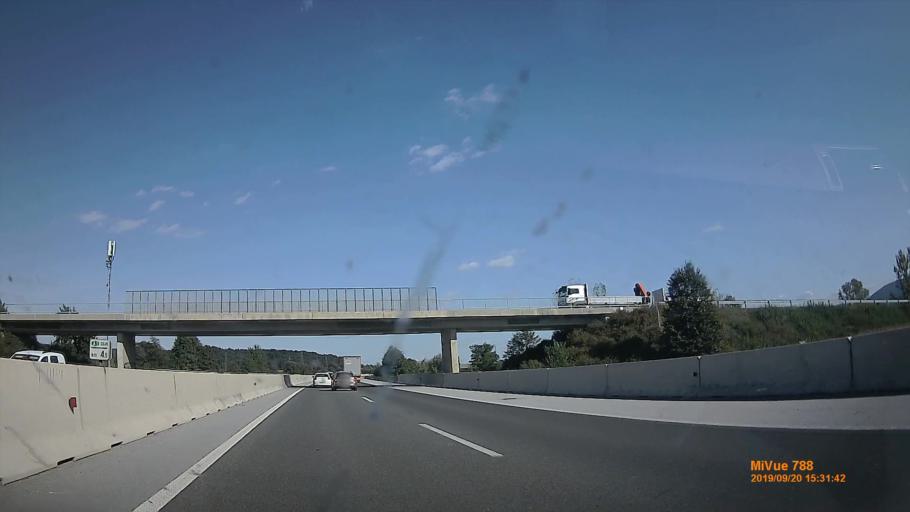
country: SI
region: Zalec
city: Sempeter v Savinj. Dolini
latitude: 46.2717
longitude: 15.1319
